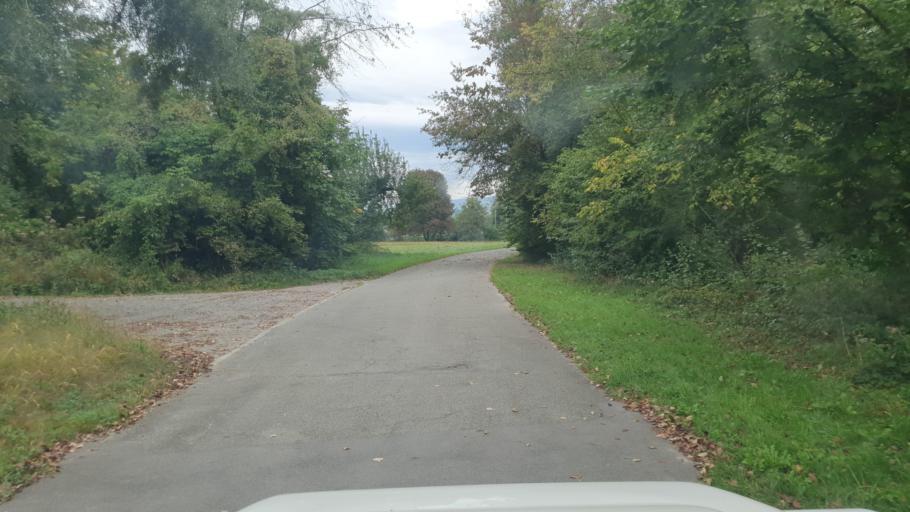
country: CH
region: Aargau
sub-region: Bezirk Bremgarten
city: Bremgarten
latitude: 47.3543
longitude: 8.3323
